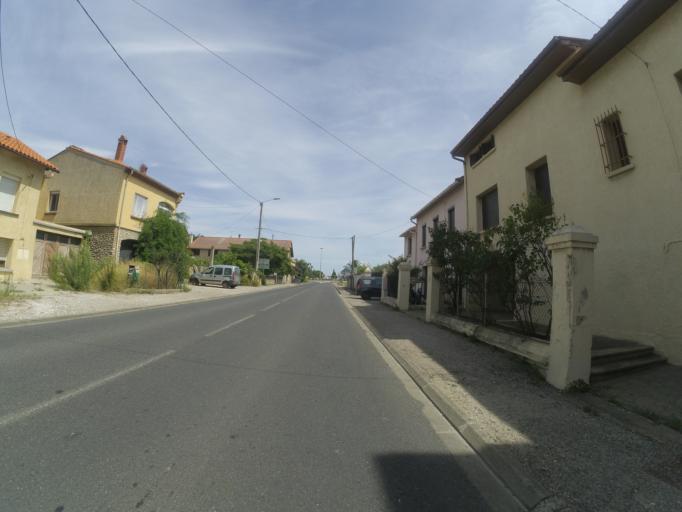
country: FR
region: Languedoc-Roussillon
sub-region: Departement des Pyrenees-Orientales
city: Ille-sur-Tet
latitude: 42.6769
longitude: 2.6311
